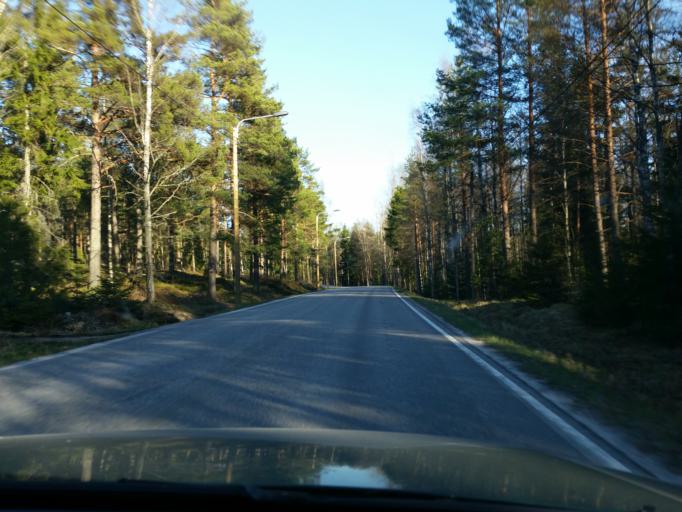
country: FI
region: Uusimaa
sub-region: Helsinki
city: Kirkkonummi
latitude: 60.1186
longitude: 24.5443
